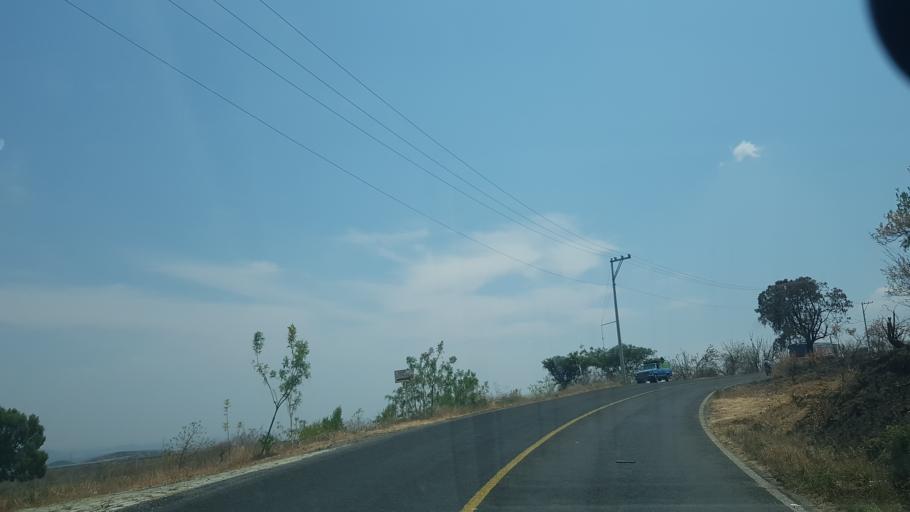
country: MX
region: Puebla
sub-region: Atzitzihuacan
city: Santiago Atzitzihuacan
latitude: 18.8343
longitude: -98.5879
